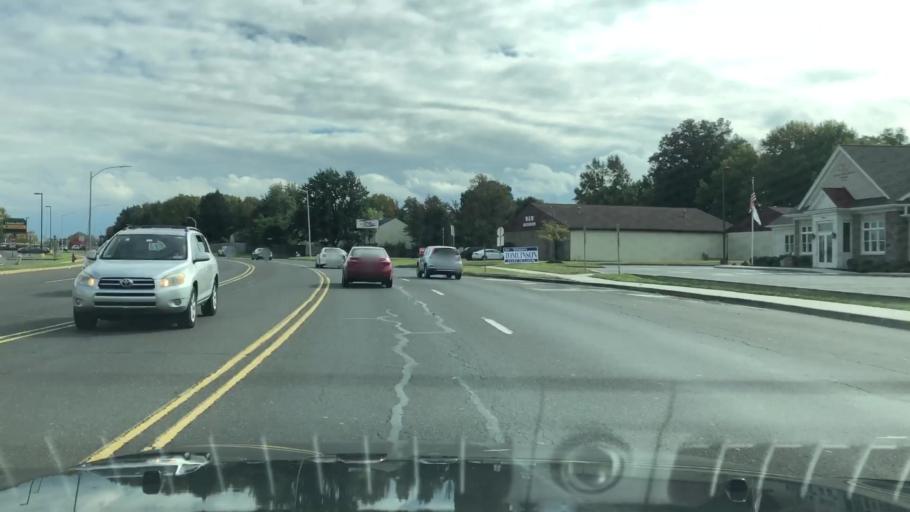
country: US
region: Pennsylvania
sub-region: Bucks County
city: Fairless Hills
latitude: 40.1690
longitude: -74.8500
